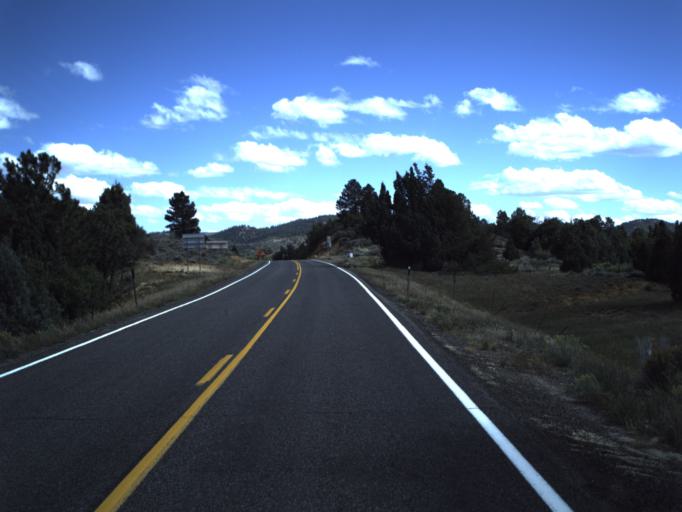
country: US
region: Utah
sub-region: Garfield County
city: Panguitch
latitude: 37.4899
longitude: -112.5187
